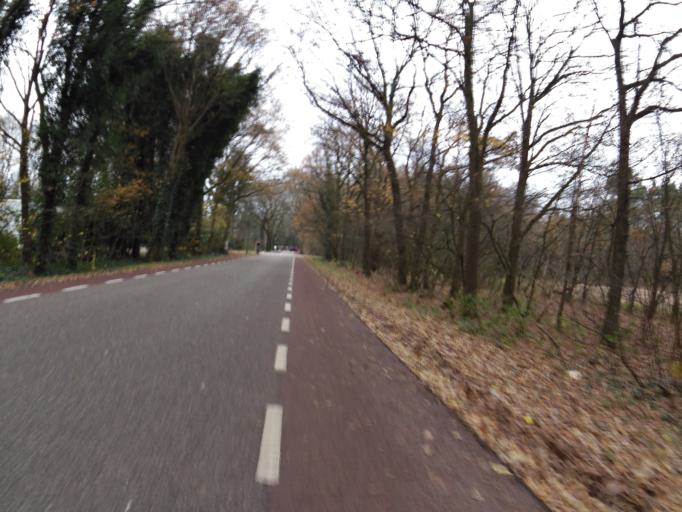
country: NL
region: North Brabant
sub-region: Gemeente Bernheze
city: Heesch
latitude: 51.7499
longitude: 5.5485
